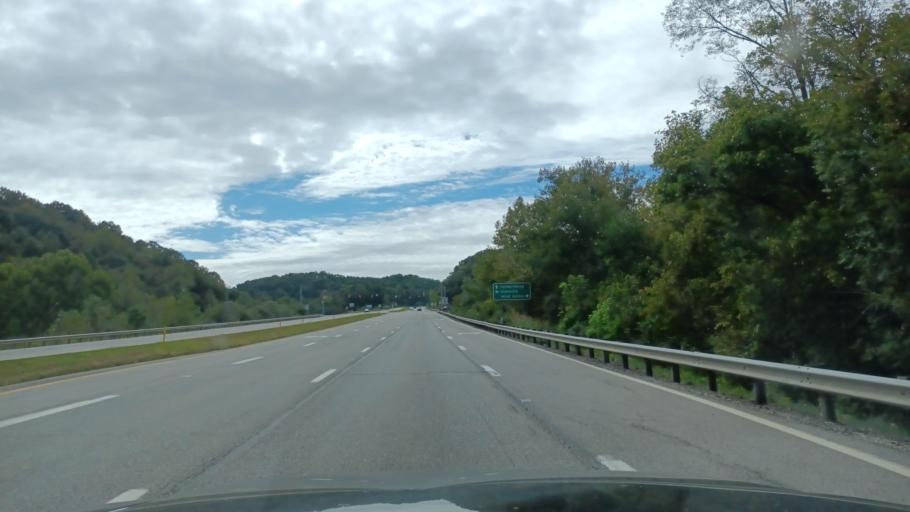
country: US
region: West Virginia
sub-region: Doddridge County
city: West Union
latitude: 39.2898
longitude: -80.7667
